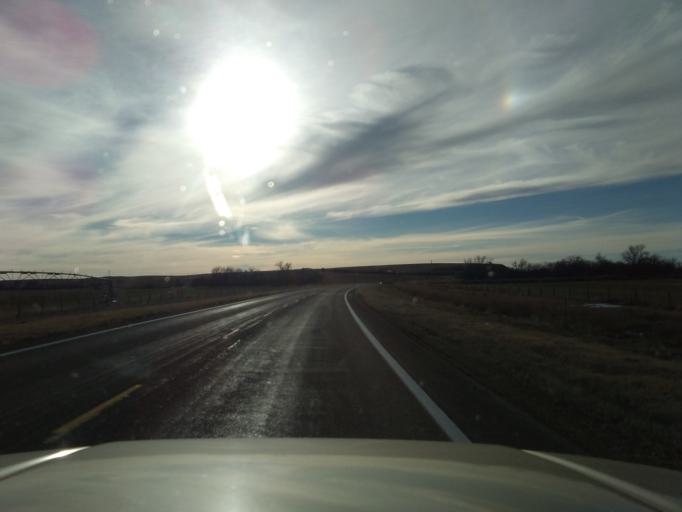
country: US
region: Kansas
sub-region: Norton County
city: Norton
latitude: 39.7242
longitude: -100.1889
